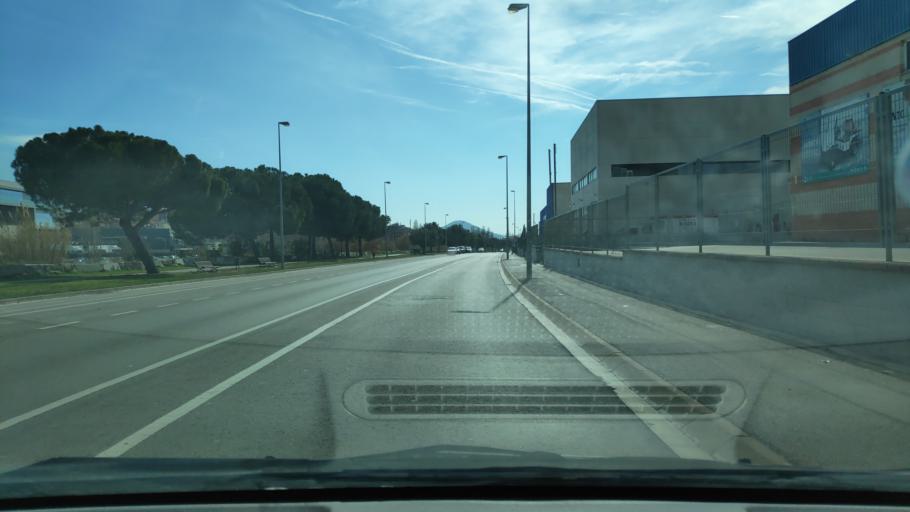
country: ES
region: Catalonia
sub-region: Provincia de Barcelona
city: Rubi
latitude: 41.5063
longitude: 2.0326
